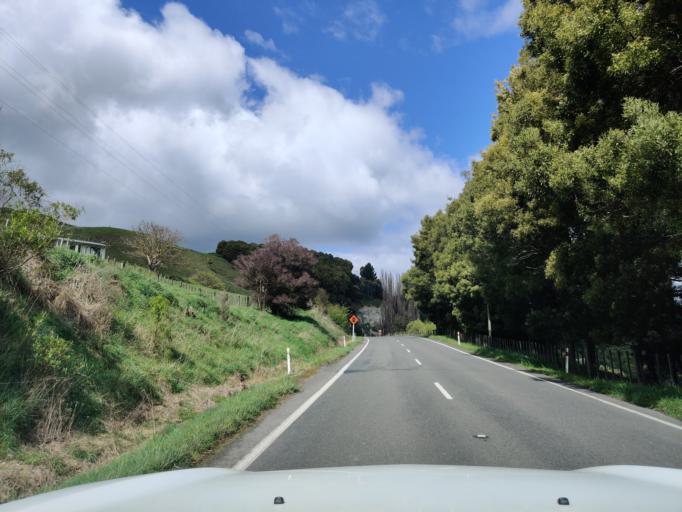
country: NZ
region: Manawatu-Wanganui
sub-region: Ruapehu District
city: Waiouru
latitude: -39.6627
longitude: 175.3327
